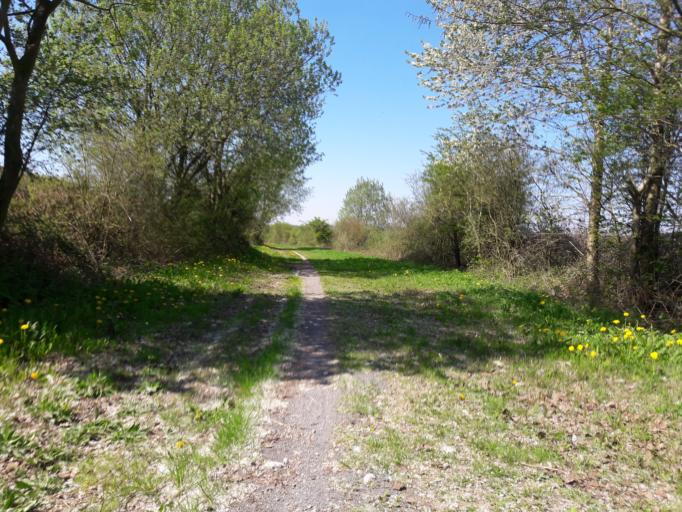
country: FR
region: Nord-Pas-de-Calais
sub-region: Departement du Nord
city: Sains-du-Nord
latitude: 50.1759
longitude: 4.0800
